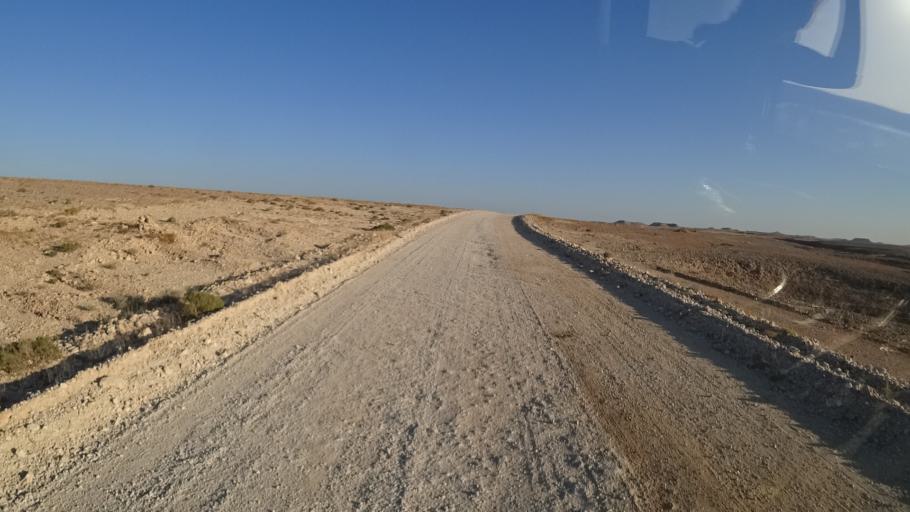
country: YE
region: Al Mahrah
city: Hawf
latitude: 17.1723
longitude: 53.3503
